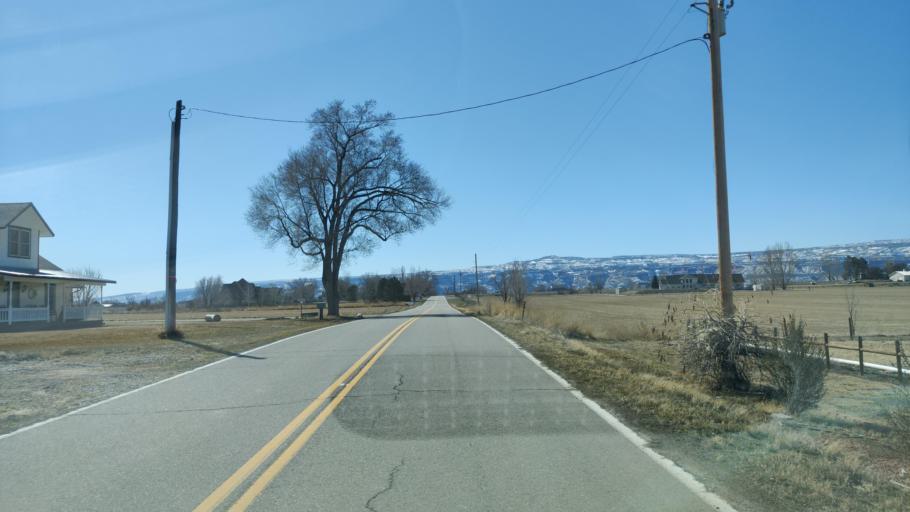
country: US
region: Colorado
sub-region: Mesa County
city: Fruita
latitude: 39.1843
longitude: -108.7197
